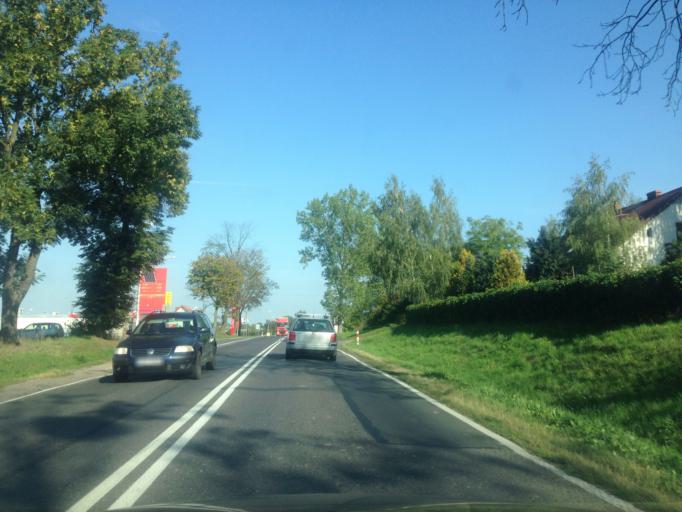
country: PL
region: Kujawsko-Pomorskie
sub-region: Powiat golubsko-dobrzynski
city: Kowalewo Pomorskie
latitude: 53.1441
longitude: 18.8674
